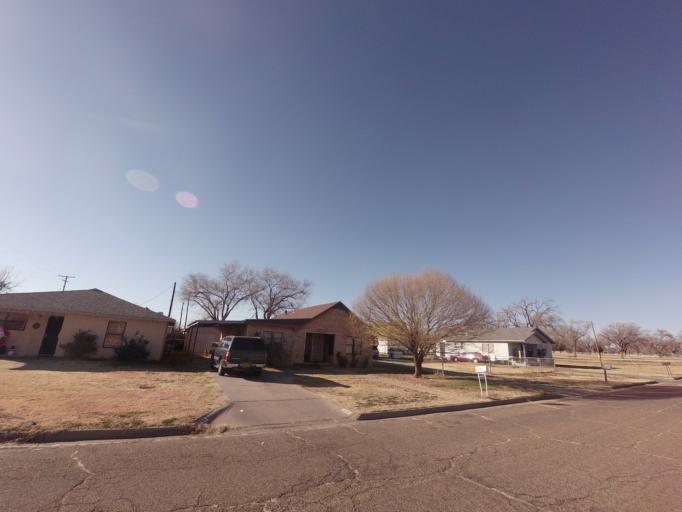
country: US
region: New Mexico
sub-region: Curry County
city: Clovis
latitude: 34.4042
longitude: -103.1826
